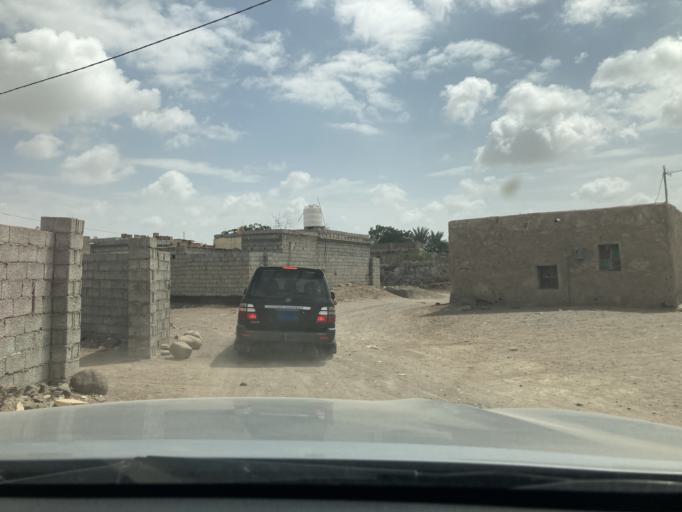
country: YE
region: Lahij
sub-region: Al  Hawtah
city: Lahij
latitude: 13.0179
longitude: 45.0033
